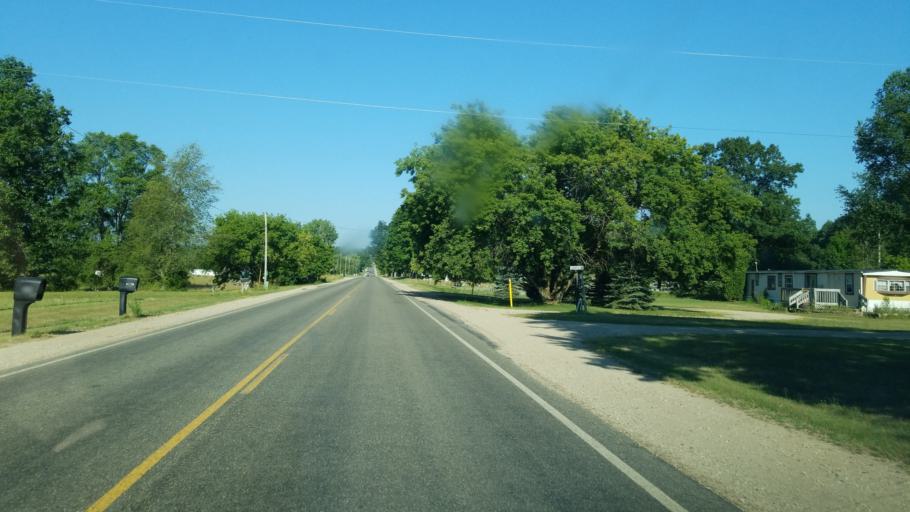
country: US
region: Michigan
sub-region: Montcalm County
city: Howard City
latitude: 43.4899
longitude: -85.4568
